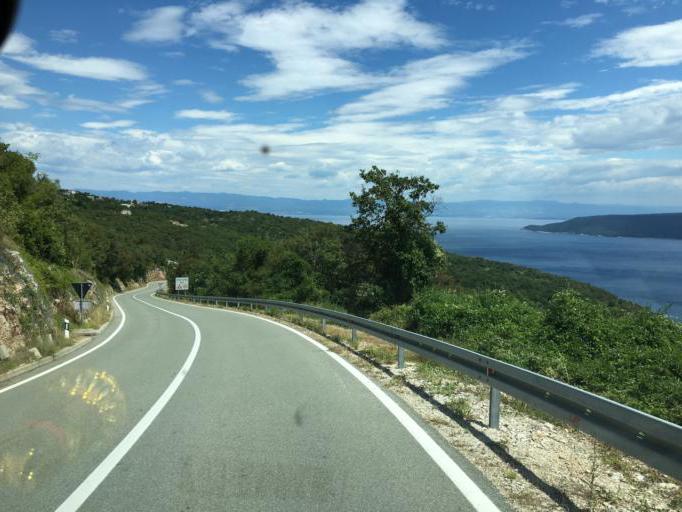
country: HR
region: Istarska
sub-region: Grad Labin
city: Rabac
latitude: 45.1546
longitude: 14.2138
